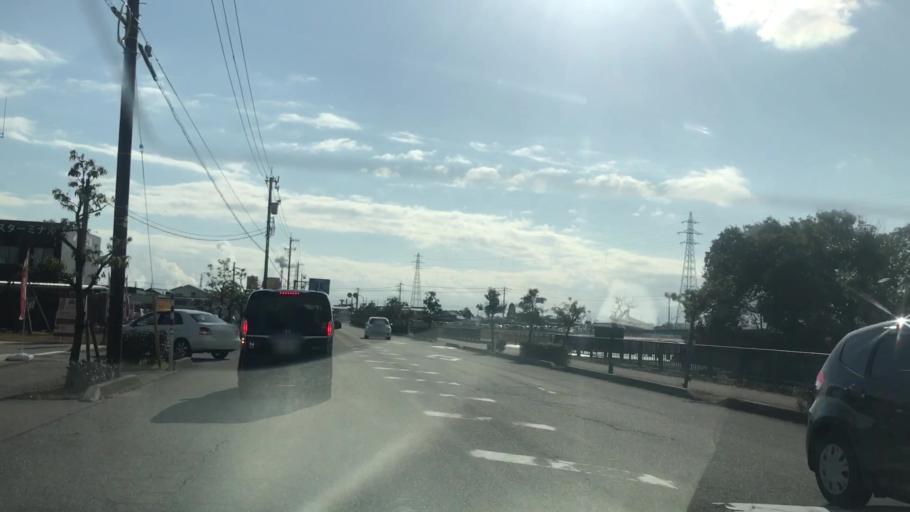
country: JP
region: Toyama
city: Takaoka
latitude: 36.7205
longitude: 137.0133
